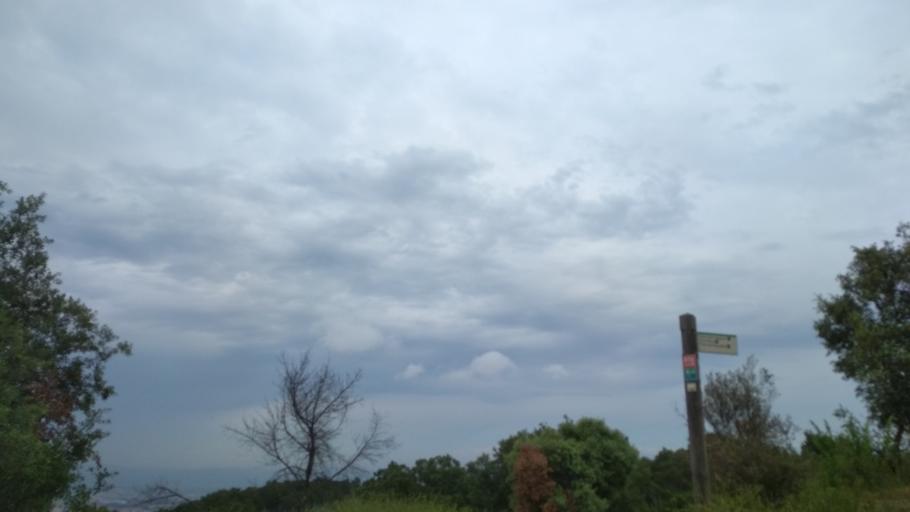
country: ES
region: Catalonia
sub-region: Provincia de Barcelona
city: Nou Barris
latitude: 41.4530
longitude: 2.1639
